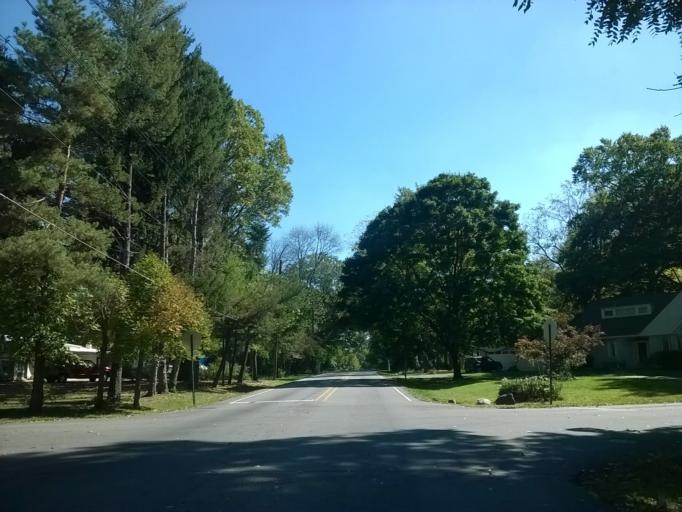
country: US
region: Indiana
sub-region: Marion County
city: Broad Ripple
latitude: 39.8632
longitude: -86.1703
